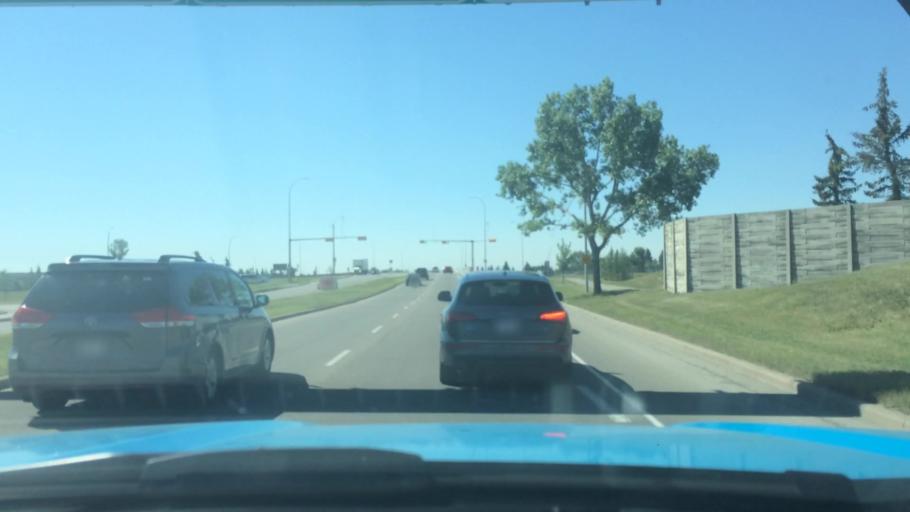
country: CA
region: Alberta
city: Calgary
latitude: 51.0694
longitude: -113.9585
